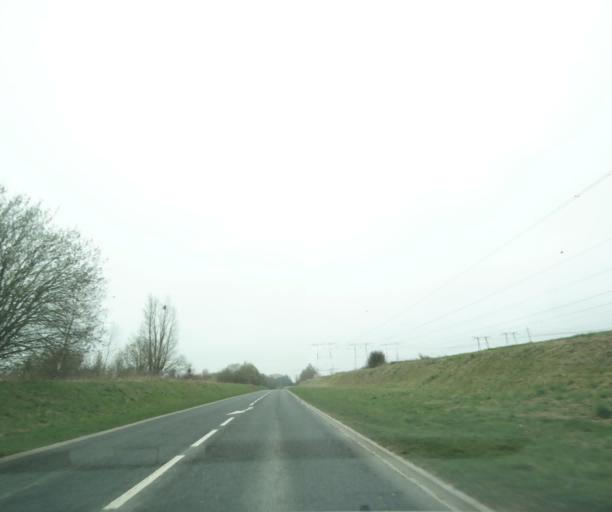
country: FR
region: Ile-de-France
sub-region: Departement du Val-d'Oise
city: Courdimanche
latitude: 49.0505
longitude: 1.9982
